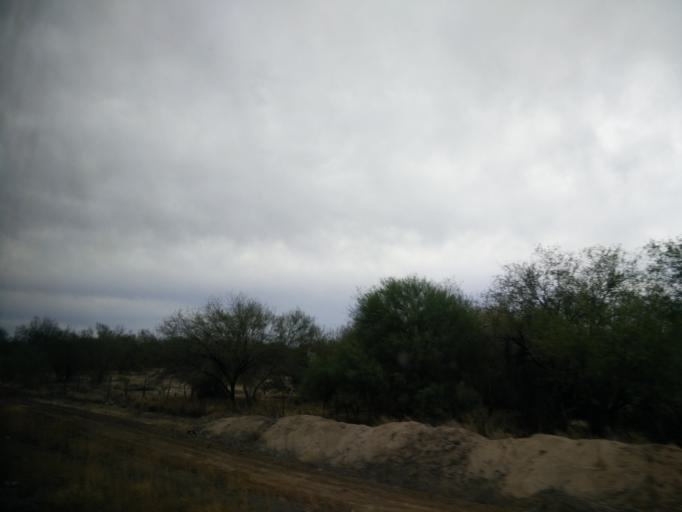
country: MX
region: Sonora
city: Hermosillo
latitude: 28.6930
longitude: -110.9890
